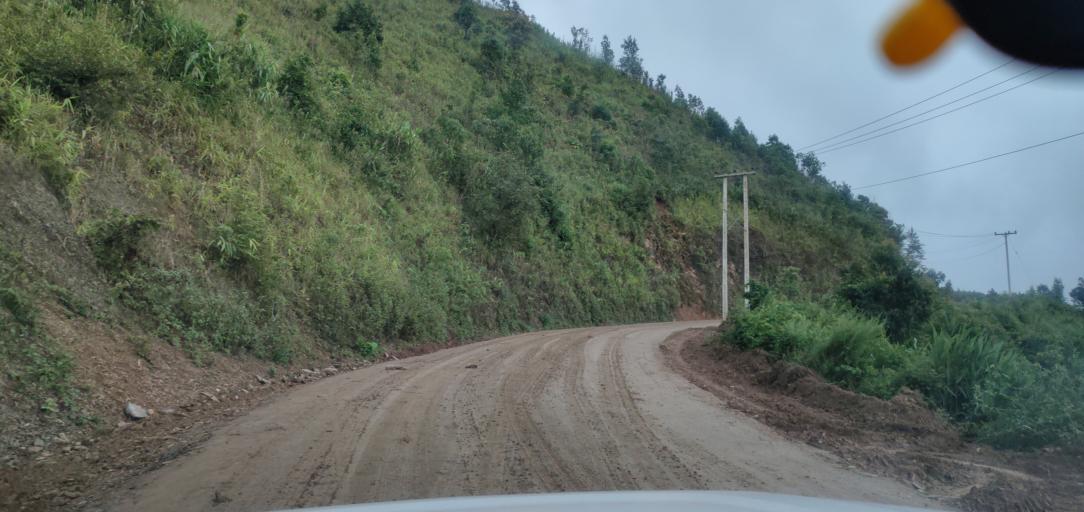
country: LA
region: Phongsali
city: Phongsali
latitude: 21.4238
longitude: 102.1735
